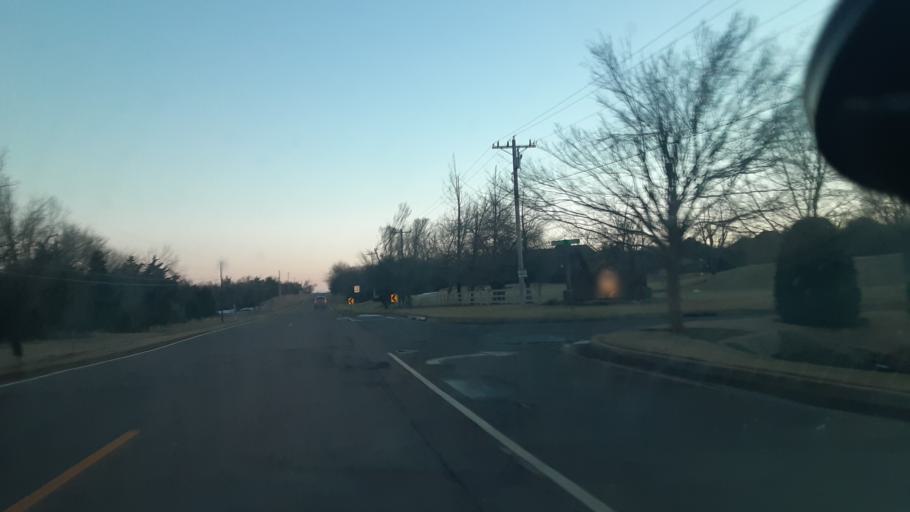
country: US
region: Oklahoma
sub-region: Oklahoma County
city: Edmond
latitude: 35.7172
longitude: -97.4252
